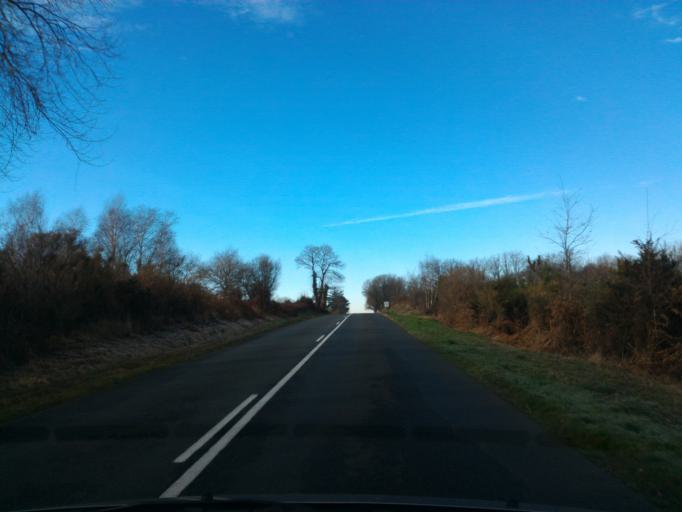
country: FR
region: Poitou-Charentes
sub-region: Departement de la Charente
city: Confolens
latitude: 46.0335
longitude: 0.5887
